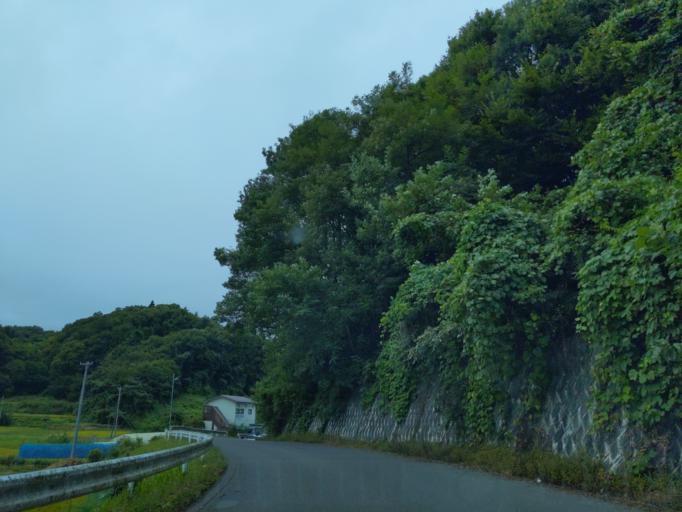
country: JP
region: Fukushima
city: Miharu
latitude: 37.3852
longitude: 140.5314
